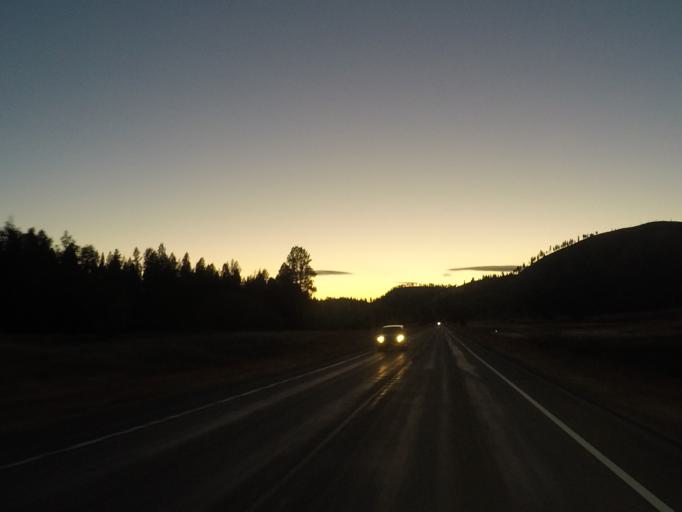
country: US
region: Montana
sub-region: Missoula County
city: Seeley Lake
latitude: 47.0306
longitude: -113.2643
